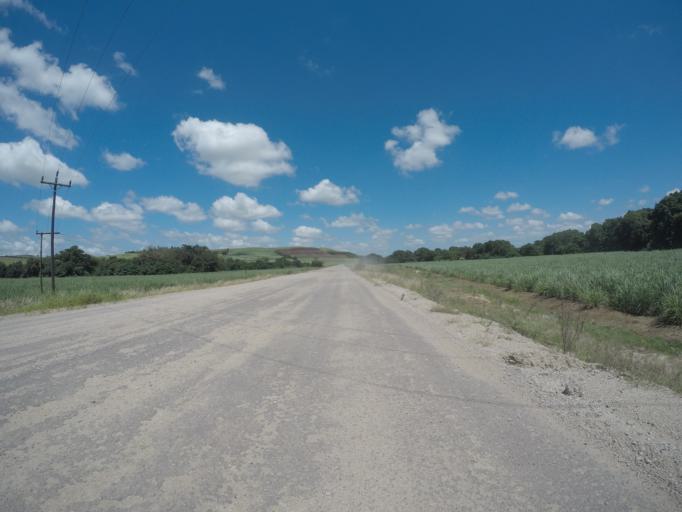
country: ZA
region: KwaZulu-Natal
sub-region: uThungulu District Municipality
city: Empangeni
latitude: -28.6431
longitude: 31.7656
